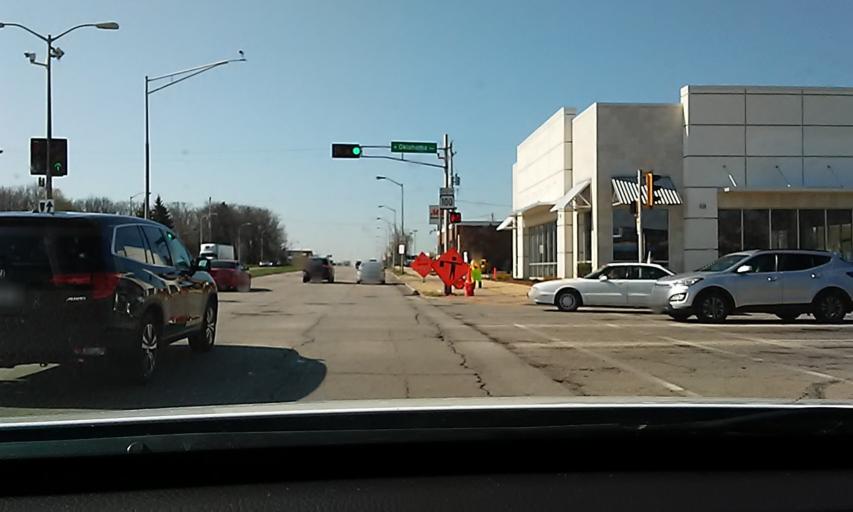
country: US
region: Wisconsin
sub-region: Milwaukee County
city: Greenfield
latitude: 42.9882
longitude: -88.0472
